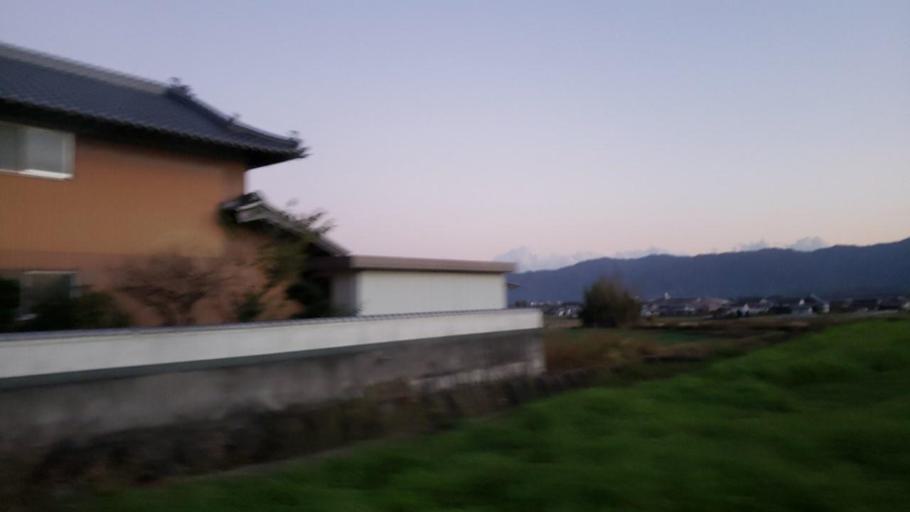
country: JP
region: Tokushima
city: Kamojimacho-jogejima
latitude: 34.1052
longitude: 134.3221
